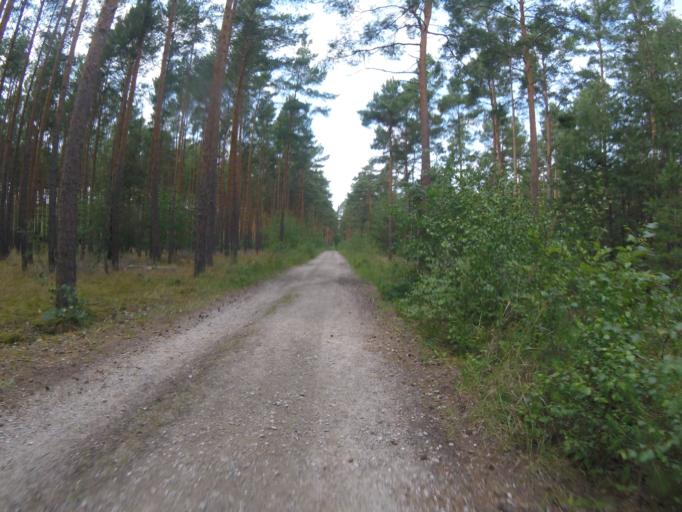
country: DE
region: Brandenburg
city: Schwerin
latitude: 52.1788
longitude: 13.6017
